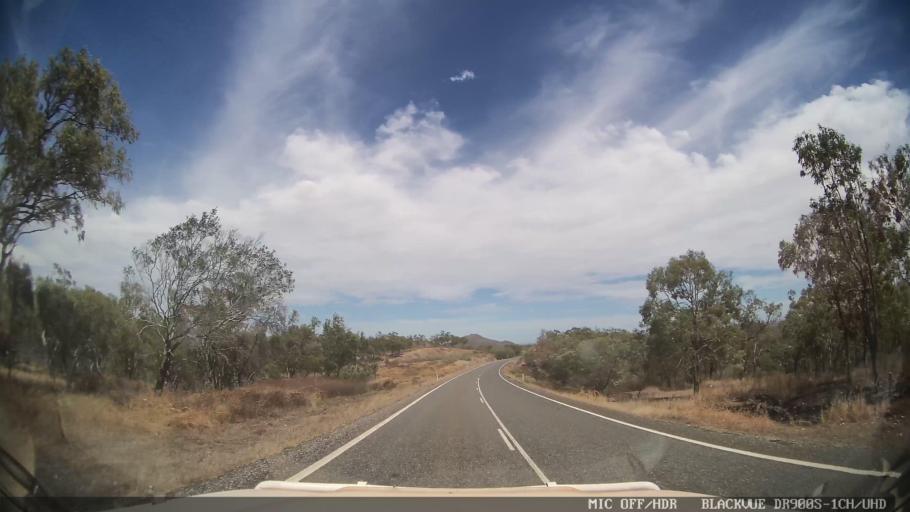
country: AU
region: Queensland
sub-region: Cook
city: Cooktown
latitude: -16.0242
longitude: 144.8112
